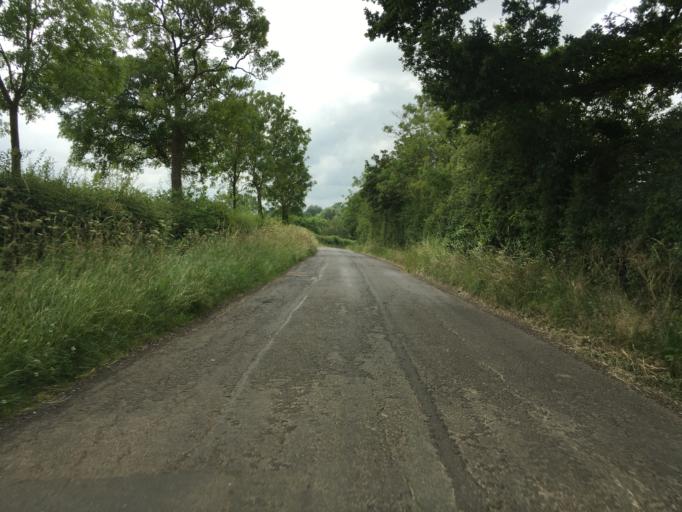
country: GB
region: England
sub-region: Oxfordshire
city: Bloxham
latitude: 51.9569
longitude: -1.3906
